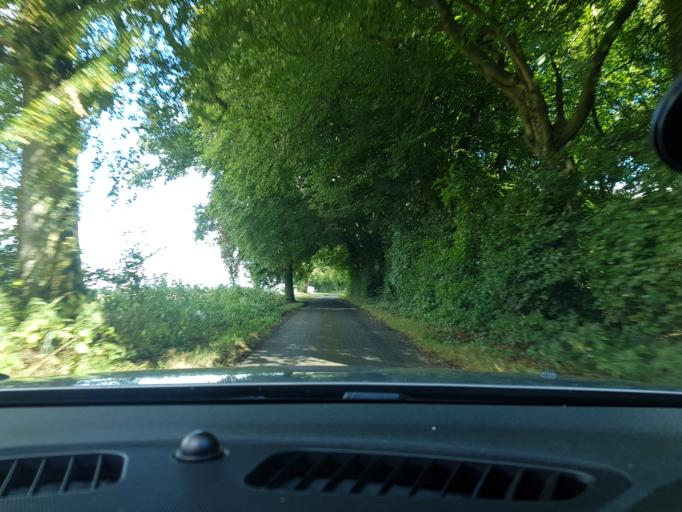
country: GB
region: England
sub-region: Wiltshire
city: Aldbourne
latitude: 51.4528
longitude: -1.6379
